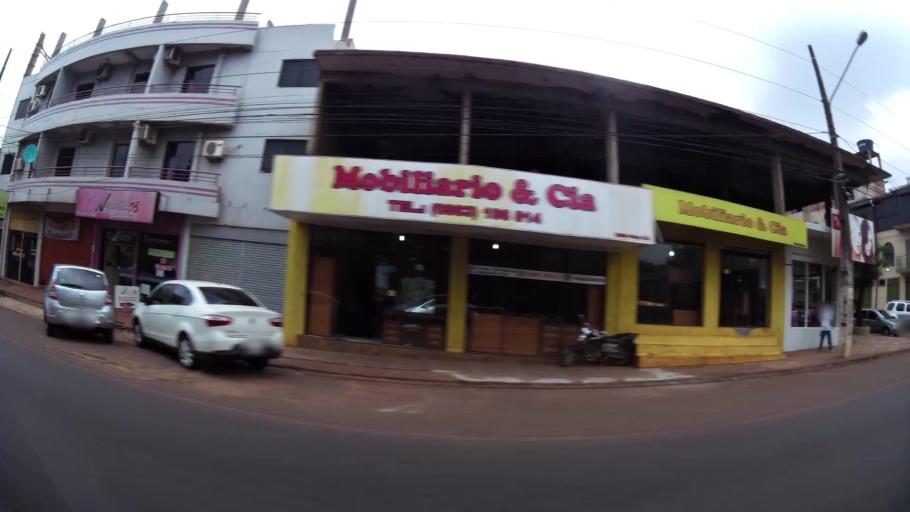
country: PY
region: Alto Parana
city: Ciudad del Este
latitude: -25.5135
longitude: -54.6415
